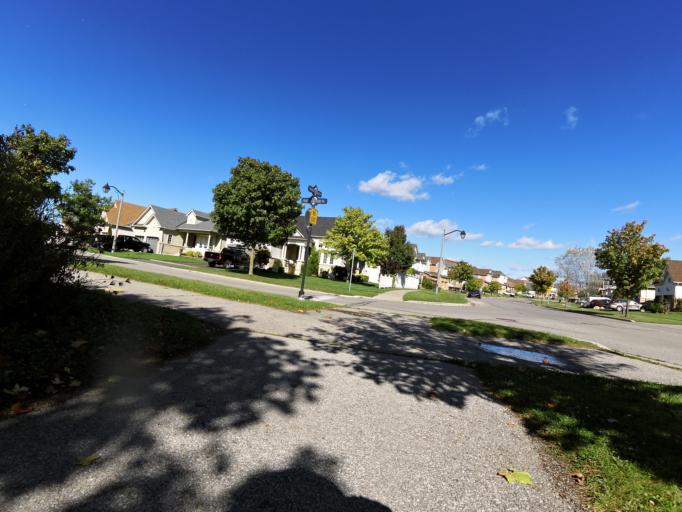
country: CA
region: Ontario
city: Ajax
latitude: 43.8554
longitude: -78.9561
